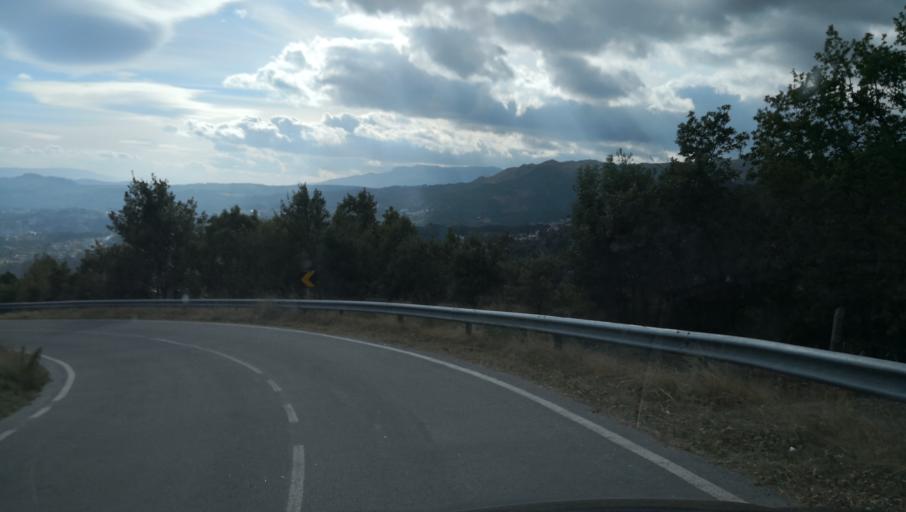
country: PT
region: Vila Real
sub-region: Vila Real
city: Vila Real
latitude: 41.3301
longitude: -7.7684
